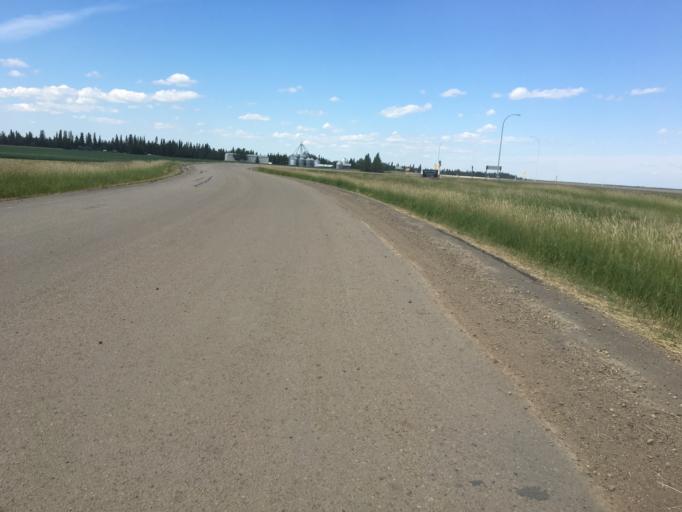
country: CA
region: Alberta
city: Spirit River
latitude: 55.7579
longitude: -118.6992
